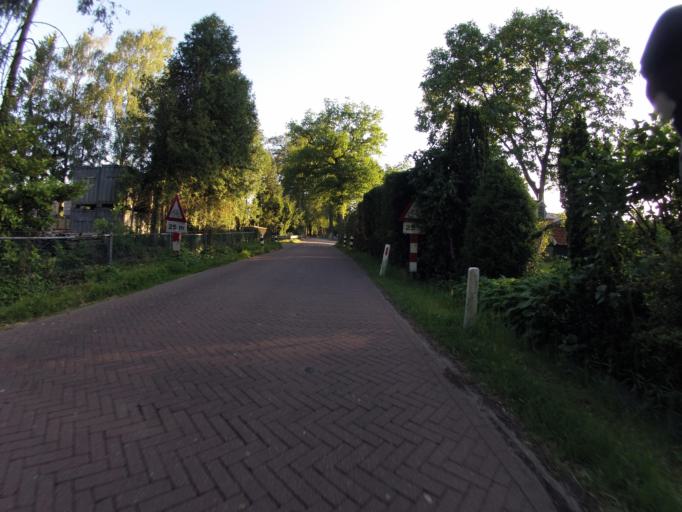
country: NL
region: Overijssel
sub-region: Gemeente Oldenzaal
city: Oldenzaal
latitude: 52.2935
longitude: 6.9479
